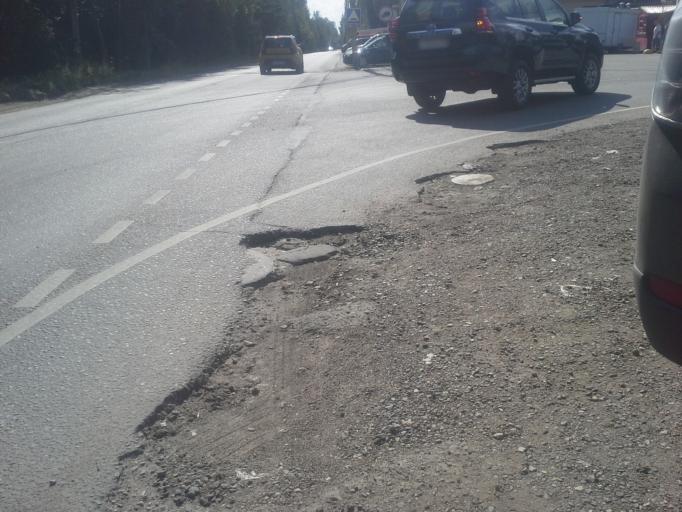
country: RU
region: Moskovskaya
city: Selyatino
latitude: 55.4739
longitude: 37.0194
